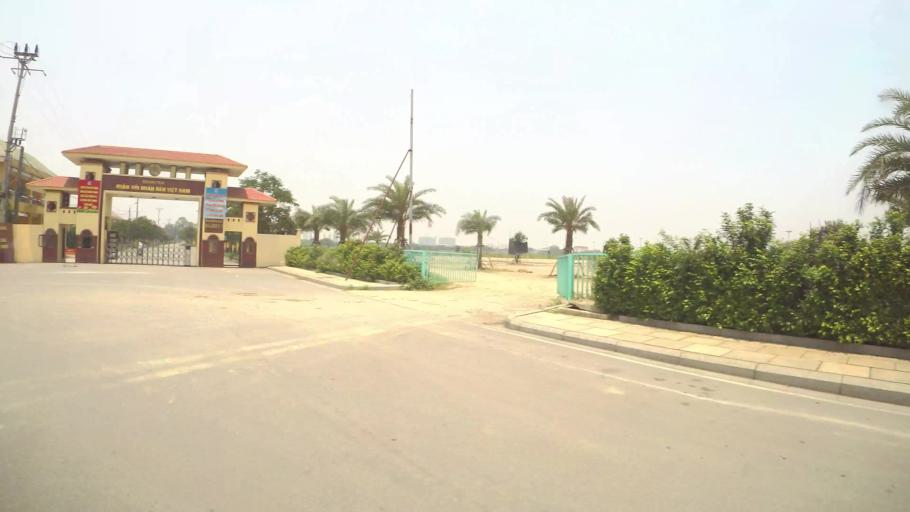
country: VN
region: Ha Noi
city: Hoan Kiem
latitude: 21.0393
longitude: 105.8941
